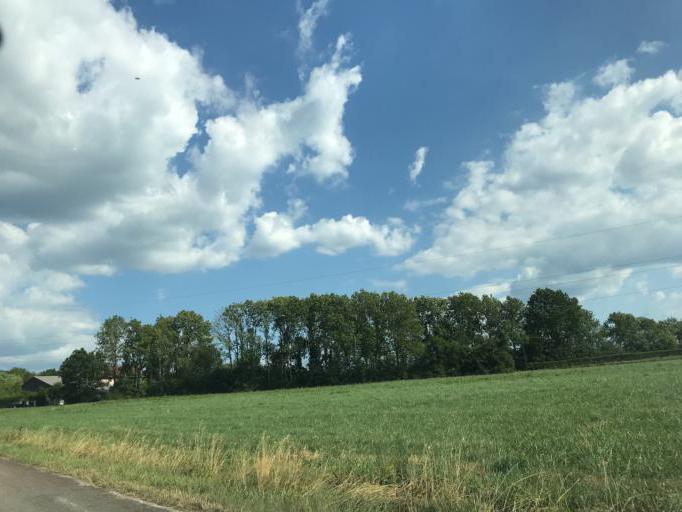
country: FR
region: Franche-Comte
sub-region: Departement du Jura
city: Clairvaux-les-Lacs
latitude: 46.5816
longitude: 5.7262
